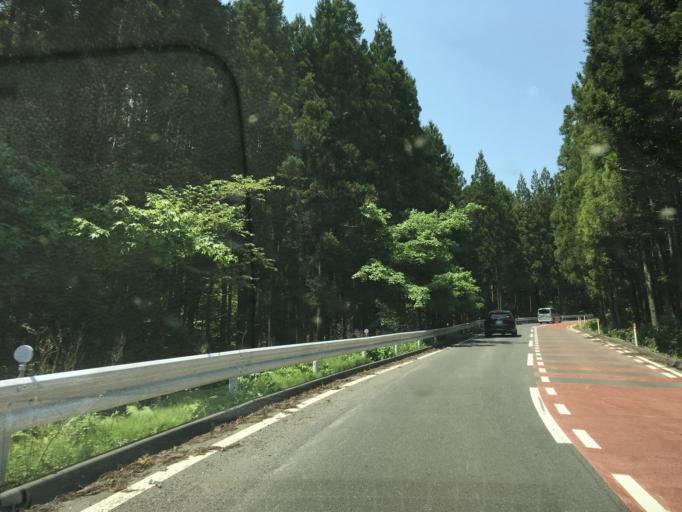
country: JP
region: Iwate
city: Ofunato
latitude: 38.8535
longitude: 141.4876
